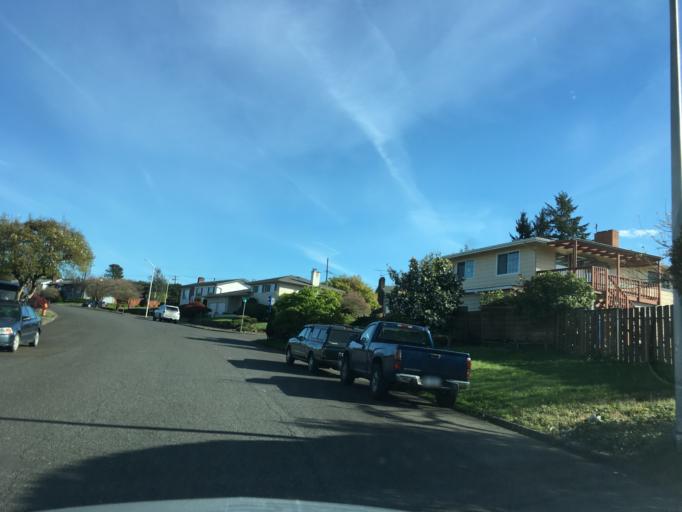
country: US
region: Oregon
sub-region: Multnomah County
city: Lents
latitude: 45.5460
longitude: -122.5238
